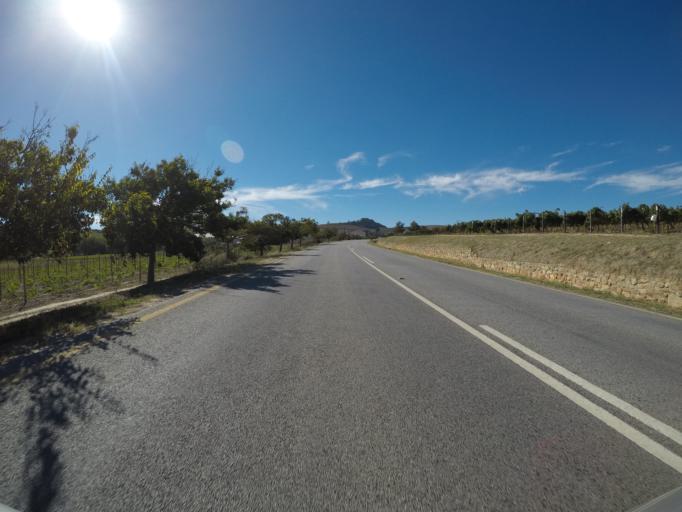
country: ZA
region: Western Cape
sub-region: City of Cape Town
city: Kraaifontein
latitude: -33.9675
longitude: 18.7453
